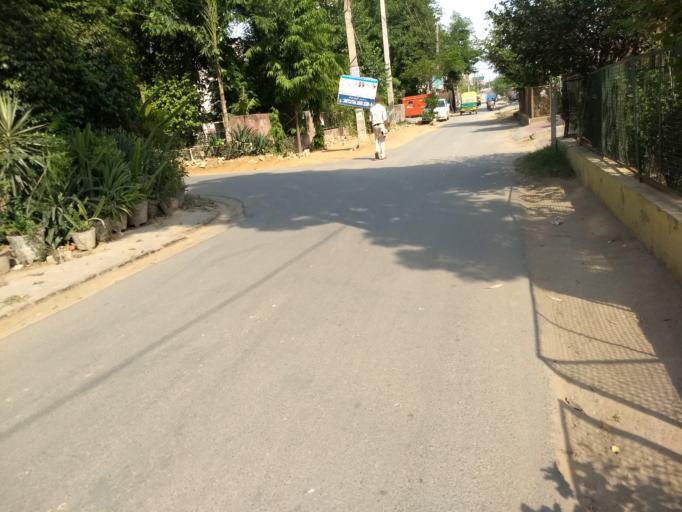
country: IN
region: Haryana
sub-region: Gurgaon
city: Gurgaon
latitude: 28.4371
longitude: 77.0472
